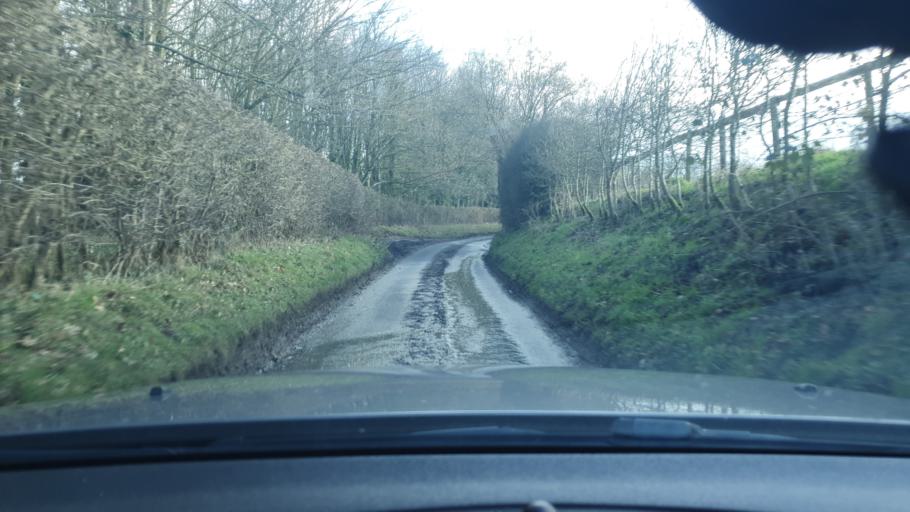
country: GB
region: England
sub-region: Wokingham
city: Wargrave
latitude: 51.5253
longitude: -0.8417
